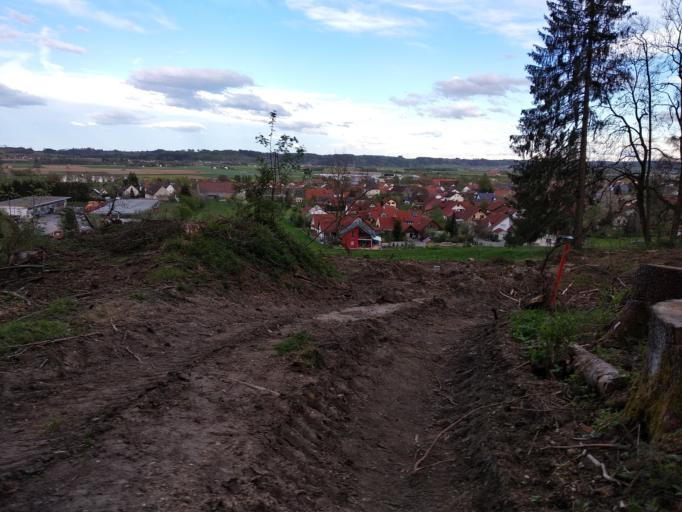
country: DE
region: Bavaria
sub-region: Swabia
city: Woringen
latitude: 47.9265
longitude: 10.1939
